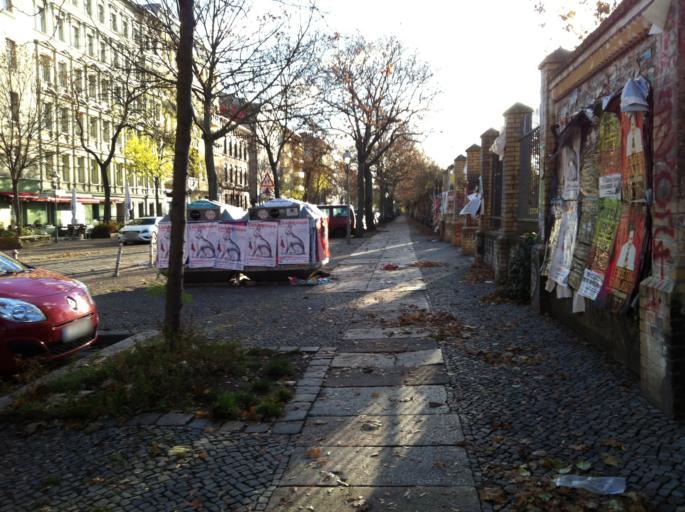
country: DE
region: Berlin
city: Berlin Treptow
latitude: 52.4973
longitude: 13.4381
